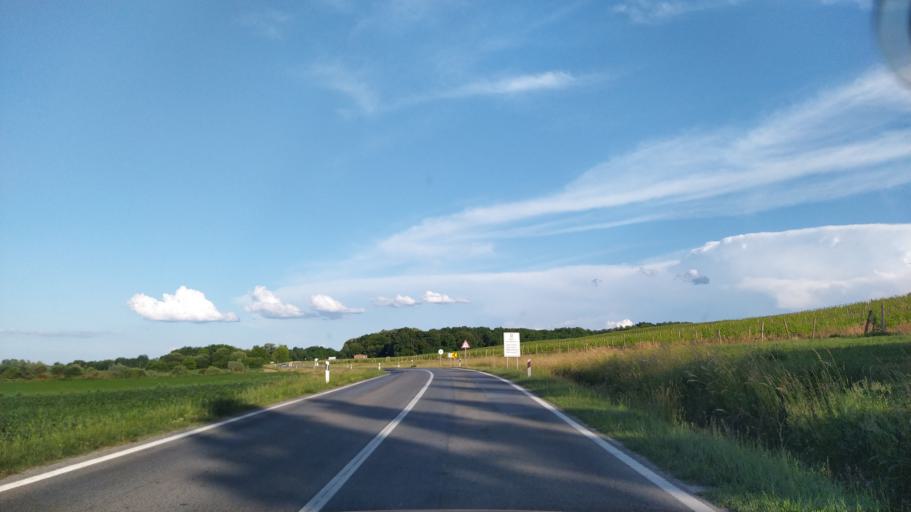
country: HR
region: Virovitick-Podravska
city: Slatina
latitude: 45.6752
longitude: 17.7532
